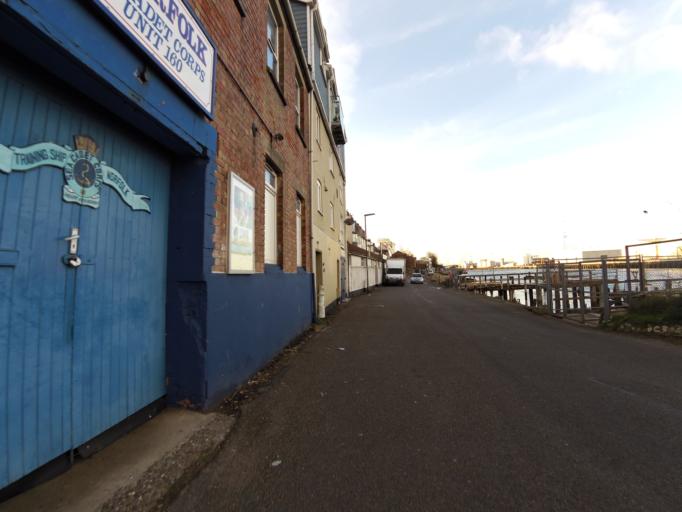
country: GB
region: England
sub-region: Norfolk
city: Gorleston-on-Sea
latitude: 52.5844
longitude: 1.7290
